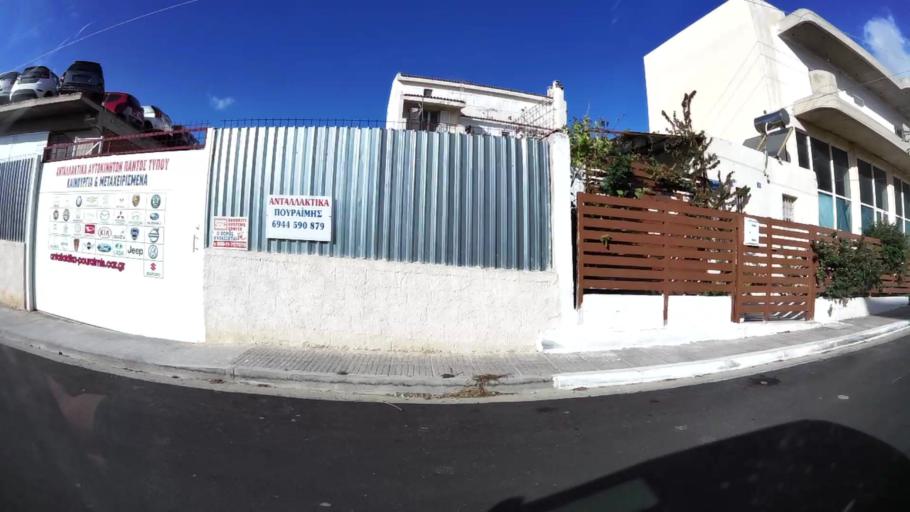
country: GR
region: Attica
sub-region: Nomarchia Anatolikis Attikis
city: Acharnes
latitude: 38.0723
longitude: 23.7438
